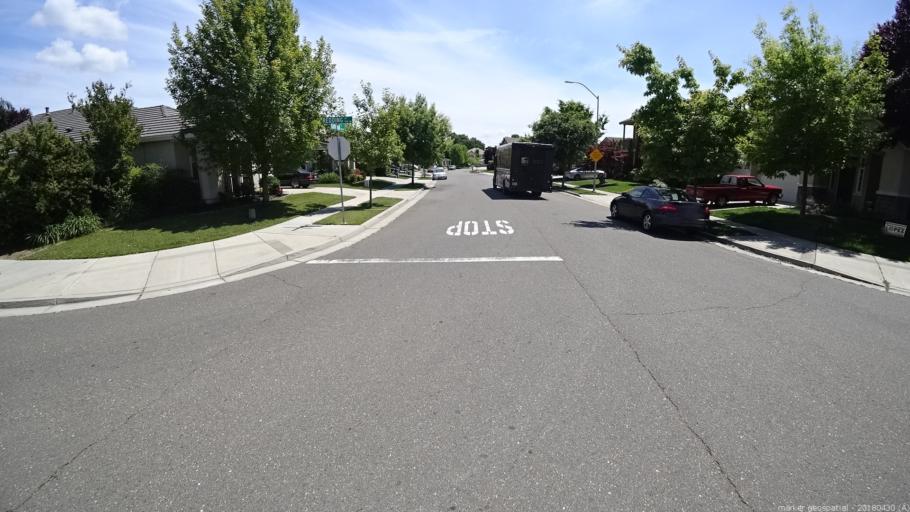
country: US
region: California
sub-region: Yolo County
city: West Sacramento
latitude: 38.5522
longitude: -121.5210
